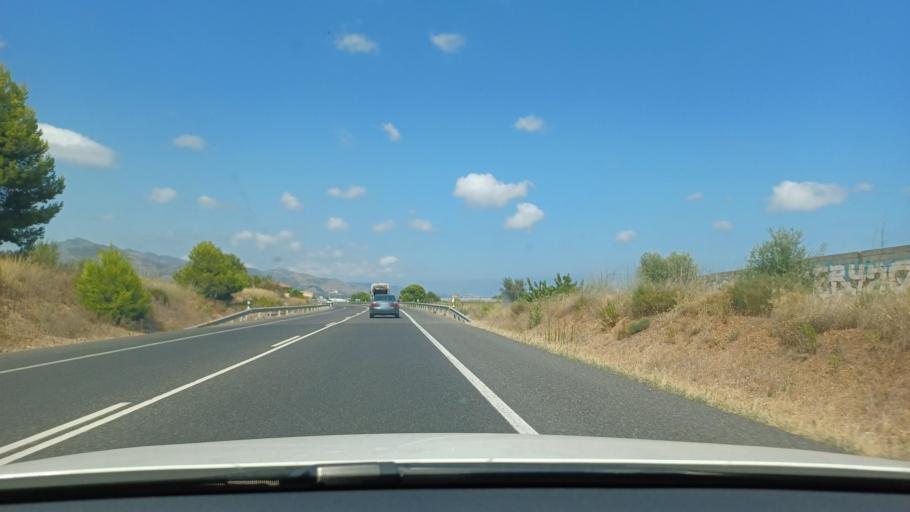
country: ES
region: Valencia
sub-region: Provincia de Castello
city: Castello de la Plana
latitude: 40.0077
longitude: -0.0556
